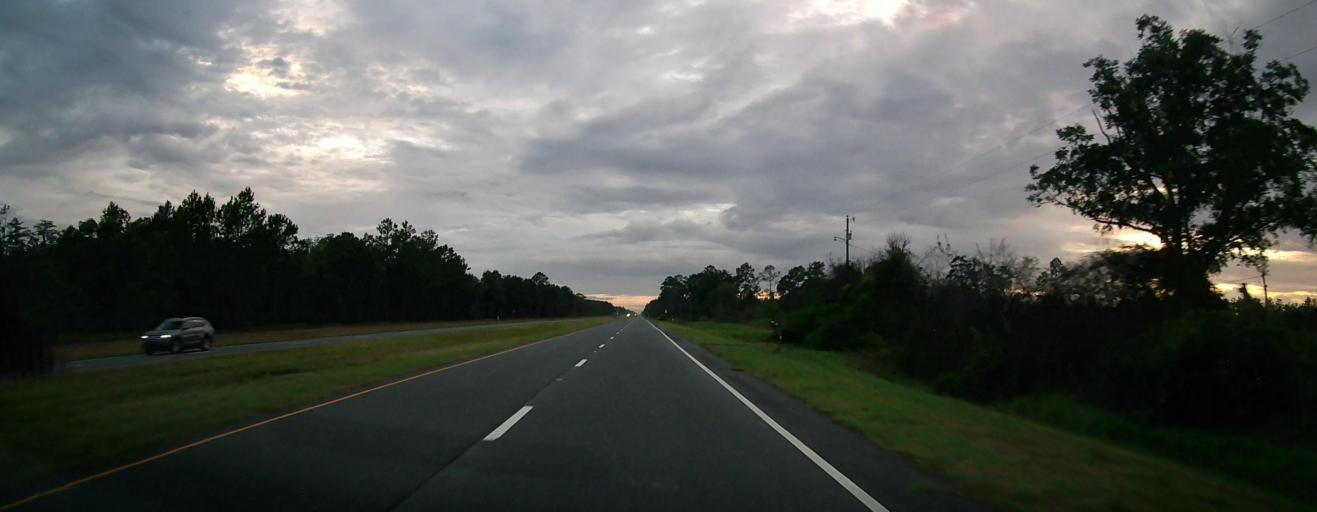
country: US
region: Georgia
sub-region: Lanier County
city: Lakeland
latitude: 30.8918
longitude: -83.1209
